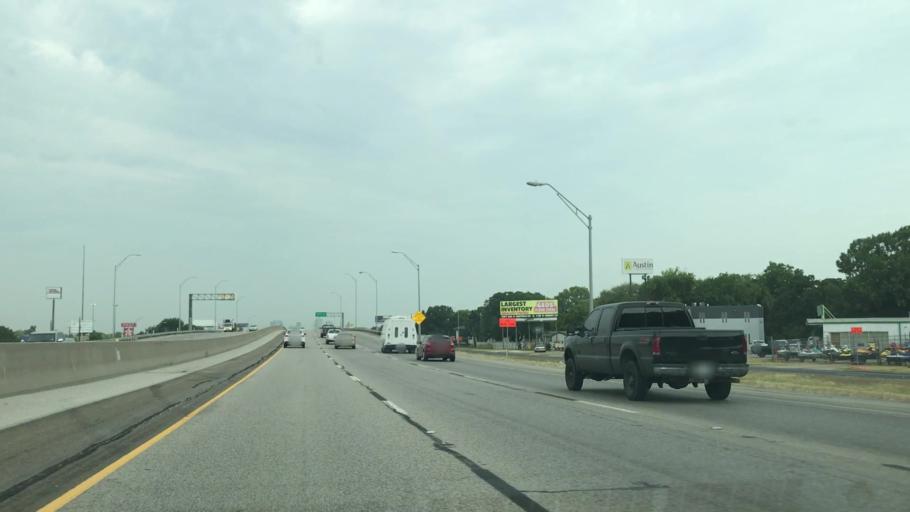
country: US
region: Texas
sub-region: Tarrant County
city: Haltom City
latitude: 32.7871
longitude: -97.2625
